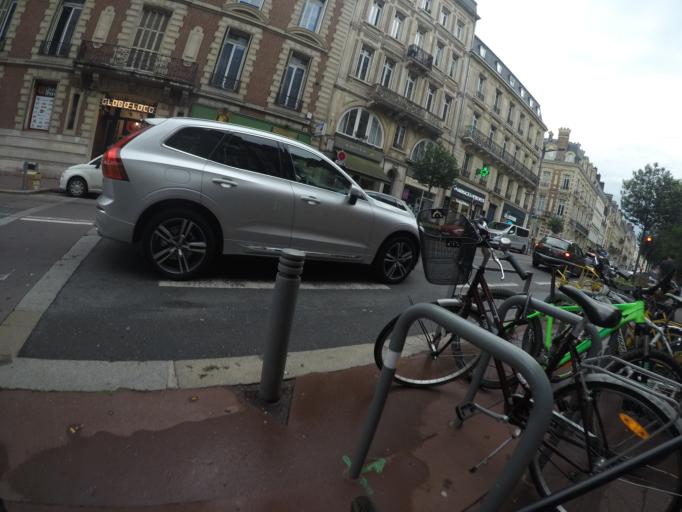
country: FR
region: Haute-Normandie
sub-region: Departement de la Seine-Maritime
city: Rouen
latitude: 49.4442
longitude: 1.0919
